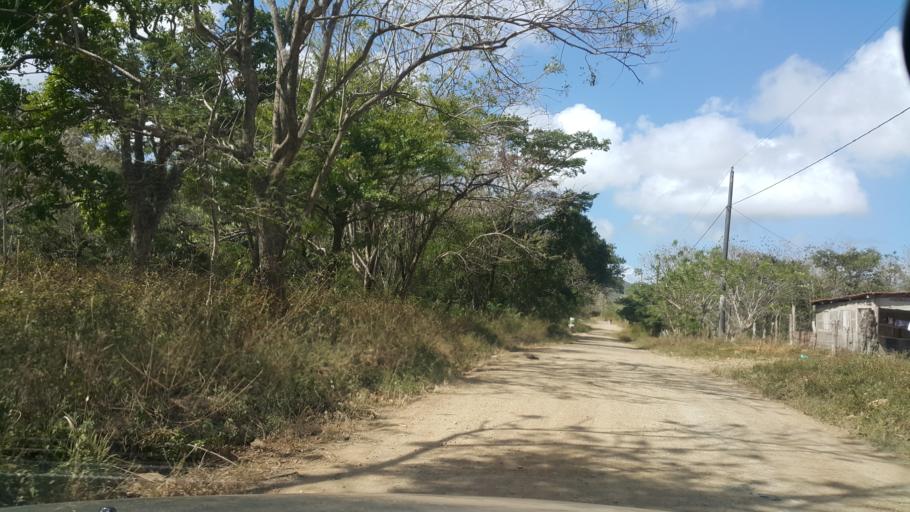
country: NI
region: Rivas
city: San Juan del Sur
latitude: 11.3082
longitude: -85.8369
